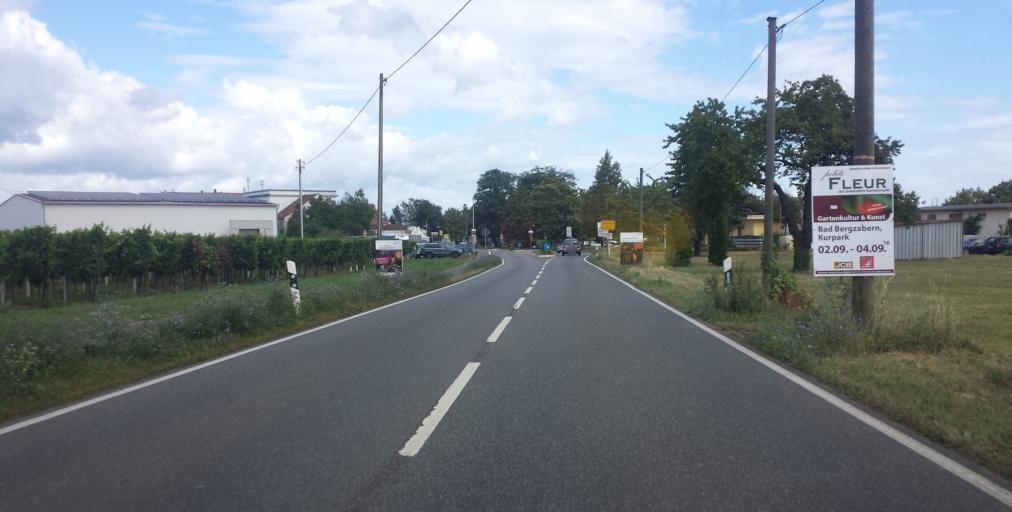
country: DE
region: Rheinland-Pfalz
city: Edenkoben
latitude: 49.2811
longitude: 8.1391
